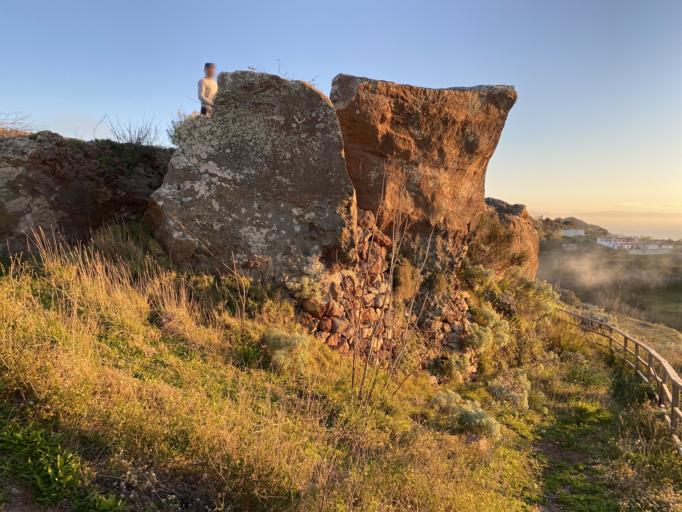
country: IT
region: Sicily
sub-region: Messina
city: Pianoconte
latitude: 38.5155
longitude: 14.9180
